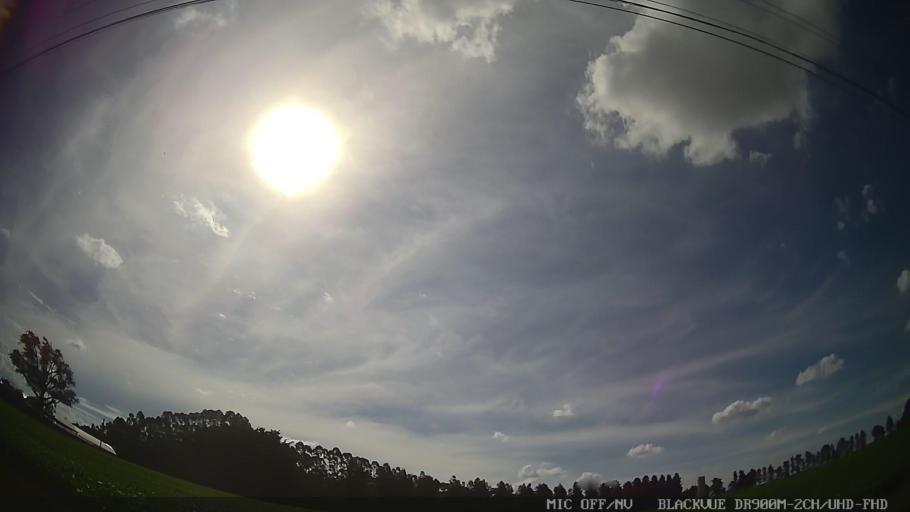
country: BR
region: Sao Paulo
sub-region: Artur Nogueira
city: Artur Nogueira
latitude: -22.6342
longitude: -47.0867
